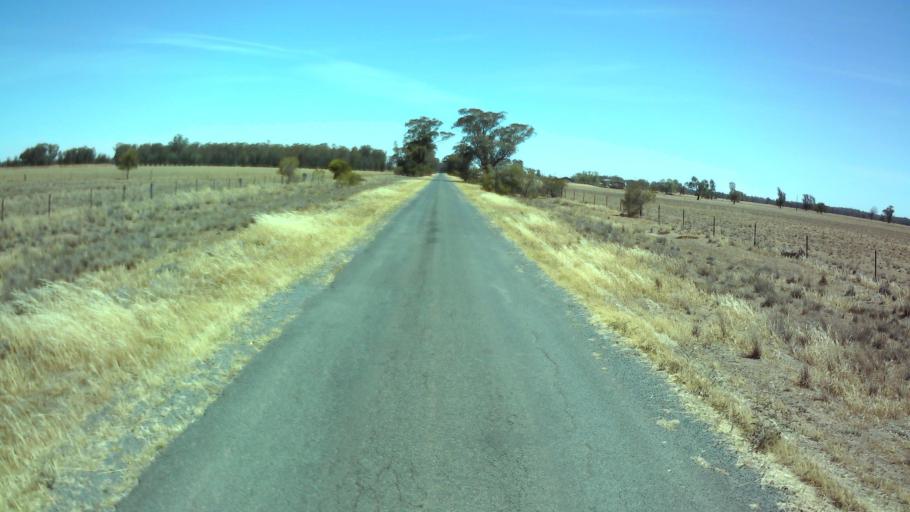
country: AU
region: New South Wales
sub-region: Weddin
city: Grenfell
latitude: -33.8987
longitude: 147.6868
